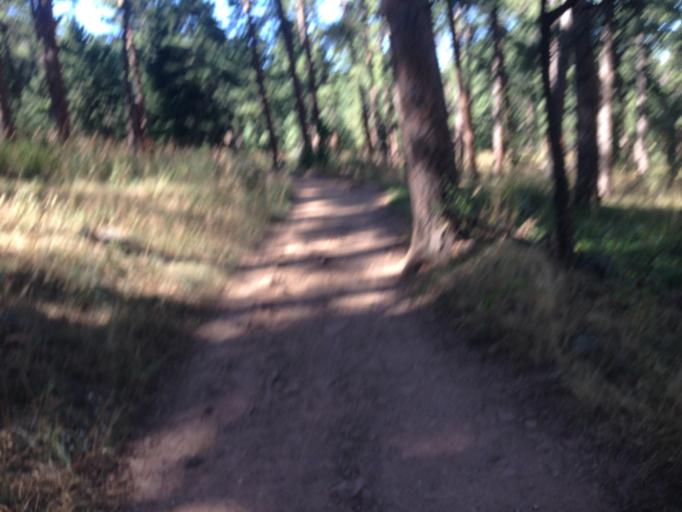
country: US
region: Colorado
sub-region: Boulder County
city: Boulder
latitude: 39.9862
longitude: -105.2859
